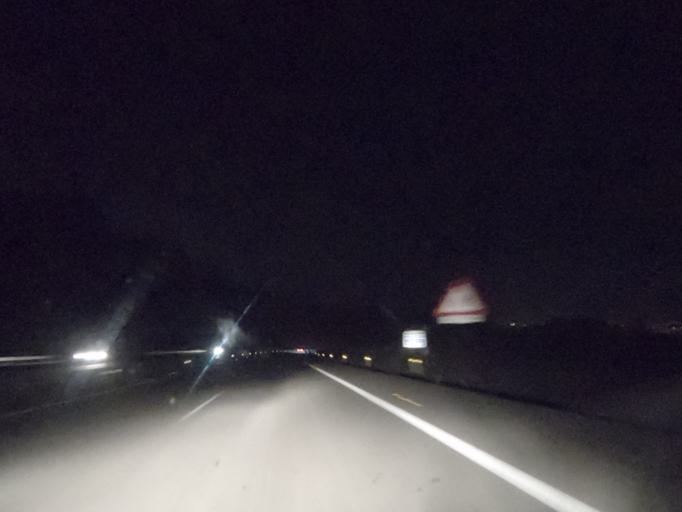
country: ES
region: Galicia
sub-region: Provincia da Coruna
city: Abegondo
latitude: 43.1820
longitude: -8.3107
